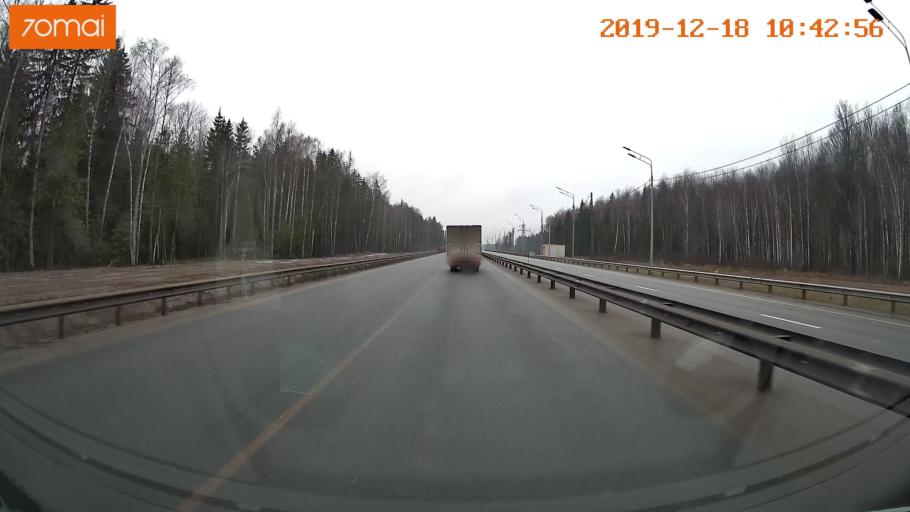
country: RU
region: Moskovskaya
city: Aprelevka
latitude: 55.4652
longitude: 37.0897
